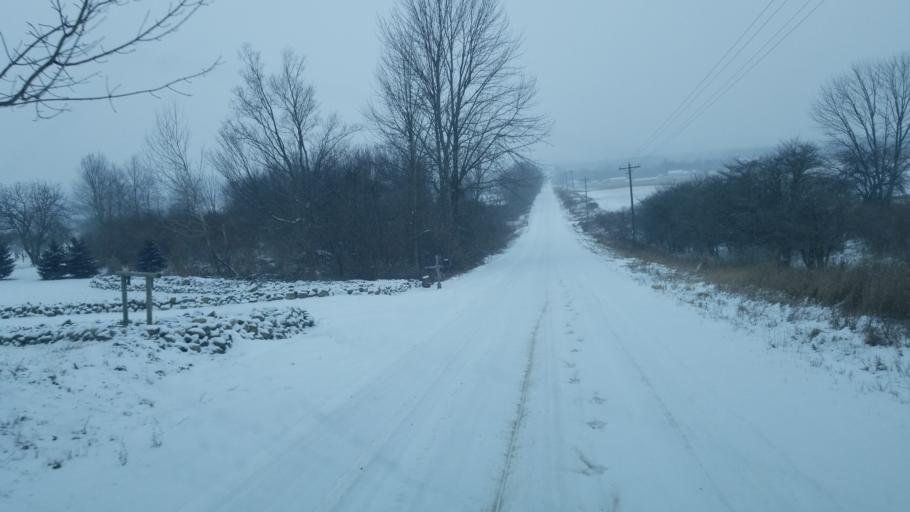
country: US
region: Michigan
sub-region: Osceola County
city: Reed City
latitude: 43.8289
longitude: -85.4048
